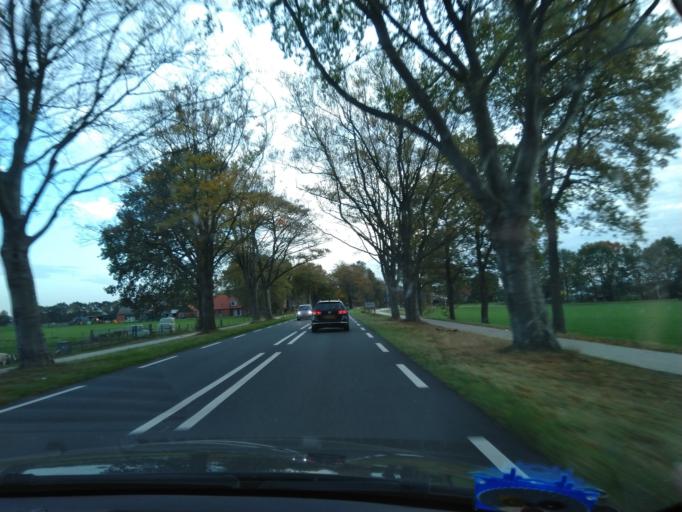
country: NL
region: Drenthe
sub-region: Gemeente Tynaarlo
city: Vries
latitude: 53.0559
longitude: 6.5756
